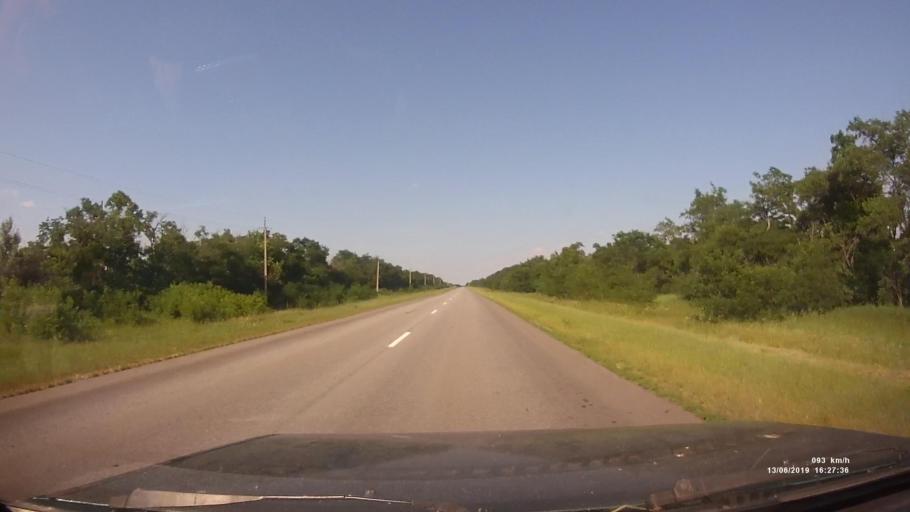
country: RU
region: Rostov
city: Kazanskaya
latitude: 49.8146
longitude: 41.1859
